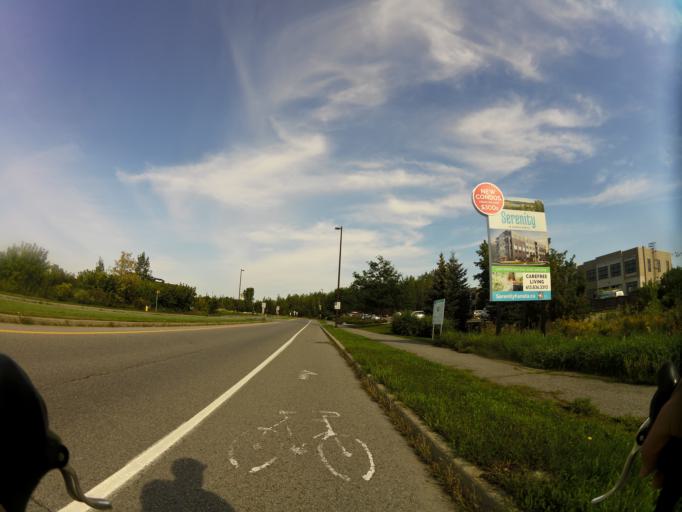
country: CA
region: Ontario
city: Bells Corners
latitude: 45.3479
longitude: -75.9032
